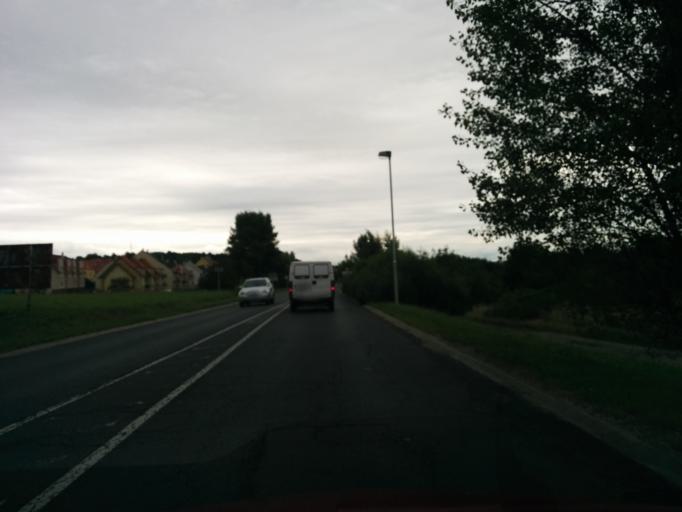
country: HU
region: Gyor-Moson-Sopron
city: Sopron
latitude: 47.6803
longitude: 16.6154
